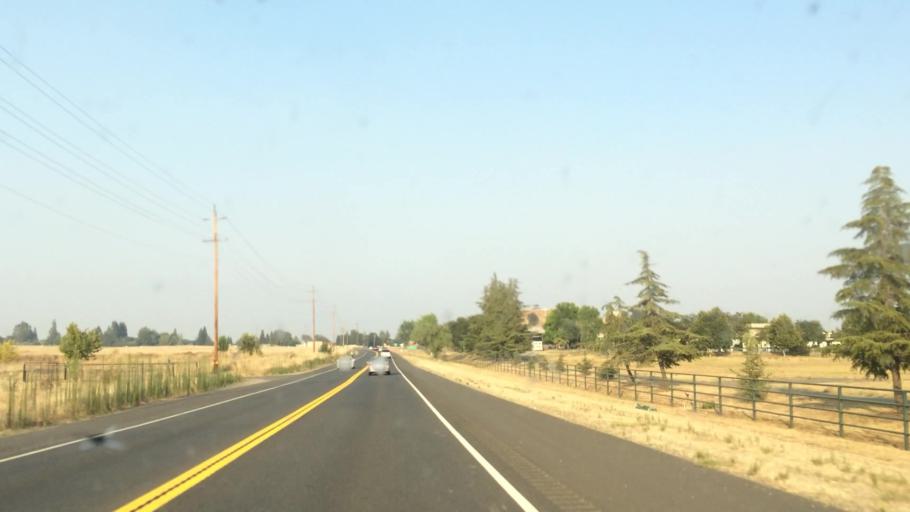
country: US
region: California
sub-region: Sacramento County
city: Rancho Murieta
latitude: 38.4966
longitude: -121.1097
